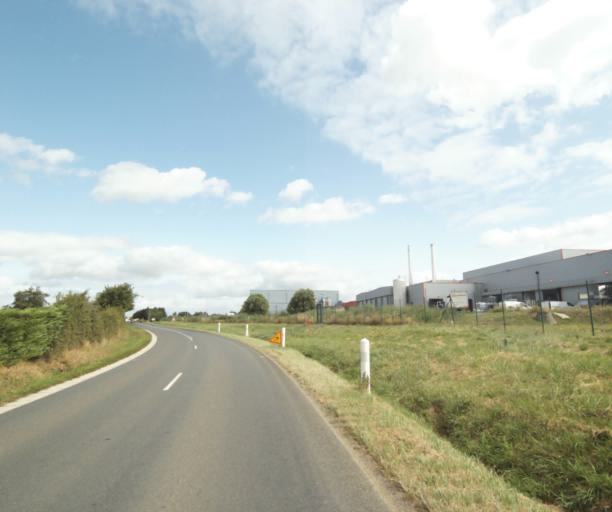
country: FR
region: Pays de la Loire
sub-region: Departement de la Sarthe
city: Sable-sur-Sarthe
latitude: 47.8237
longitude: -0.3181
